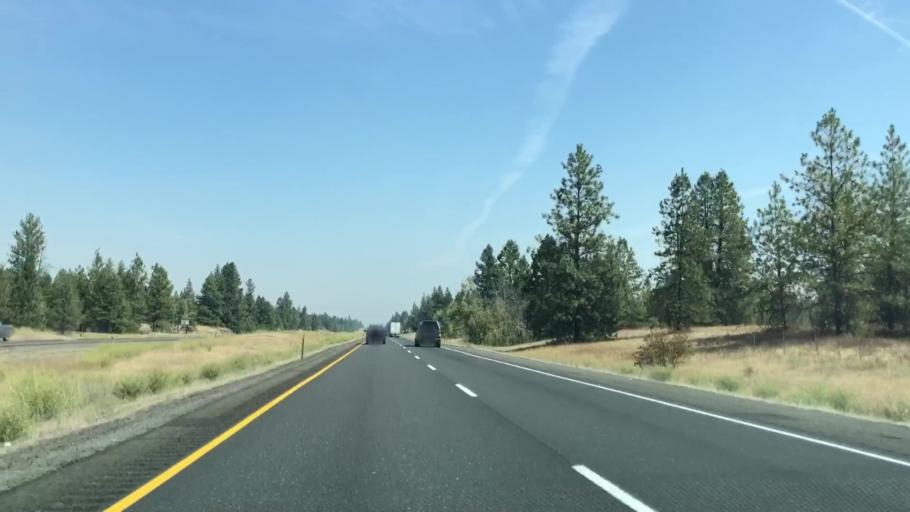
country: US
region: Washington
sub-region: Spokane County
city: Medical Lake
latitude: 47.4662
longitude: -117.7491
